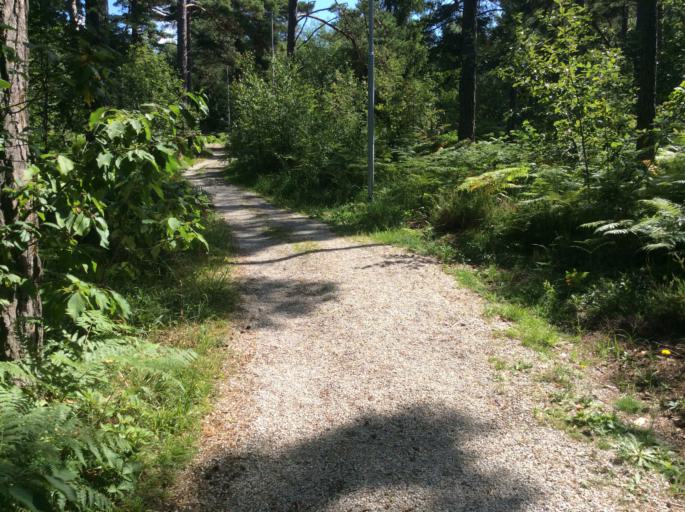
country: SE
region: Gotland
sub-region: Gotland
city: Vibble
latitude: 57.6003
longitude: 18.2725
